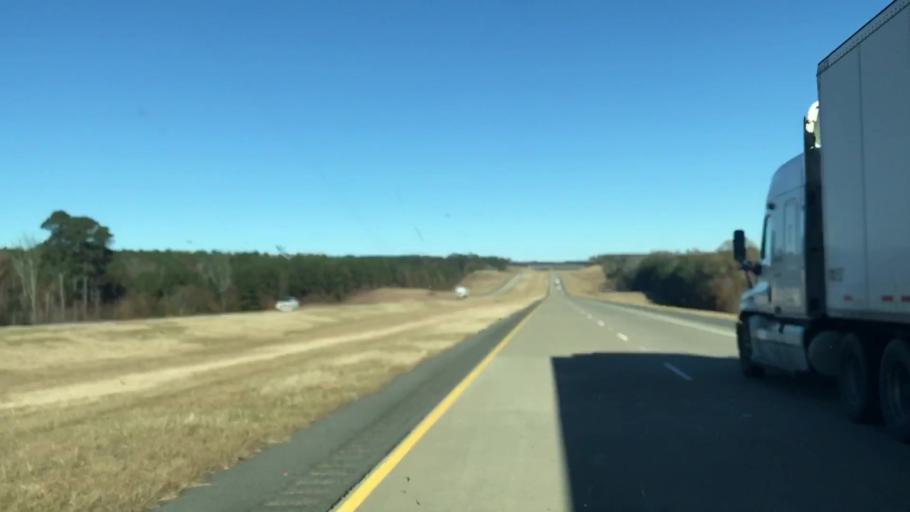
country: US
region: Louisiana
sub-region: Caddo Parish
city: Vivian
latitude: 32.9618
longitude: -93.9034
